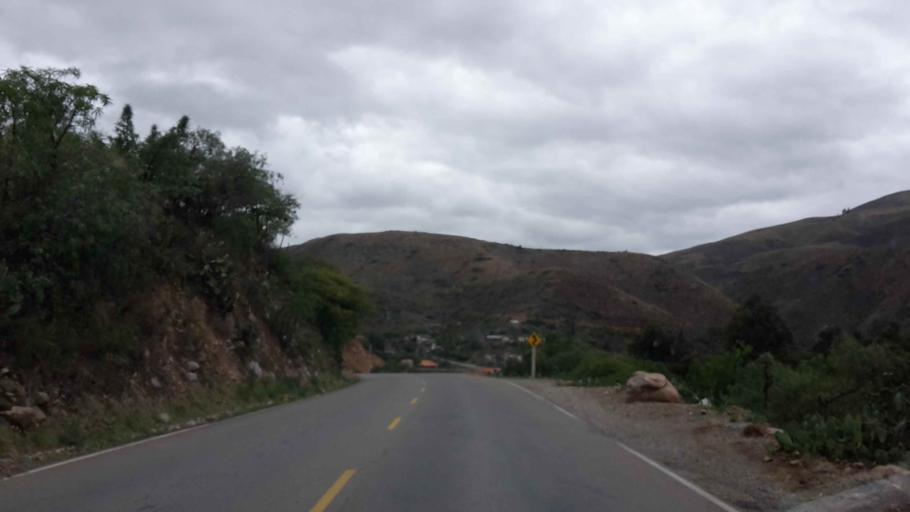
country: BO
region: Cochabamba
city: Punata
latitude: -17.5082
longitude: -65.8044
